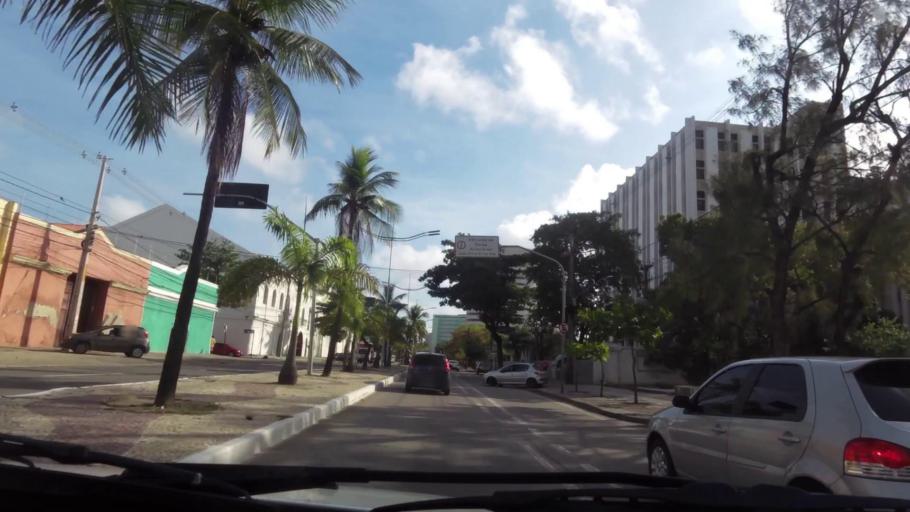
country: BR
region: Pernambuco
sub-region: Recife
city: Recife
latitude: -8.0579
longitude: -34.8725
